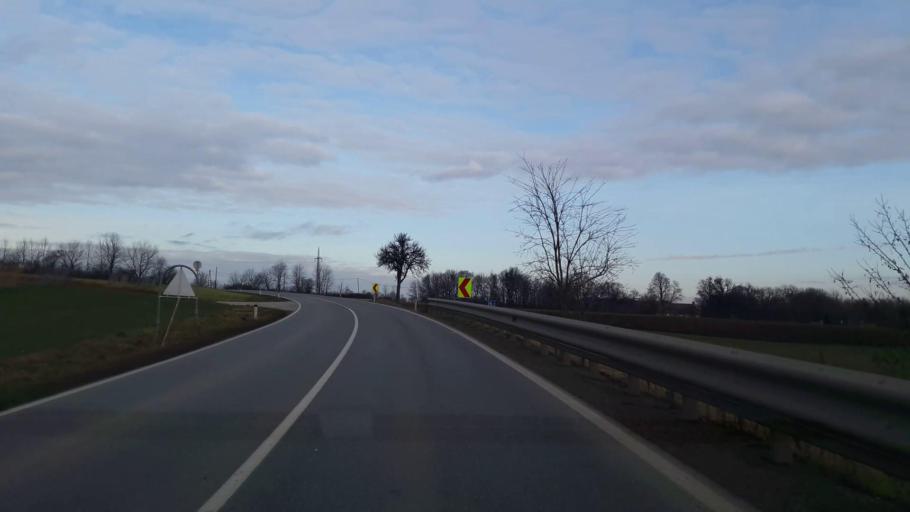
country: AT
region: Lower Austria
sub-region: Politischer Bezirk Mistelbach
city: Staatz
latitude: 48.6347
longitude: 16.5187
